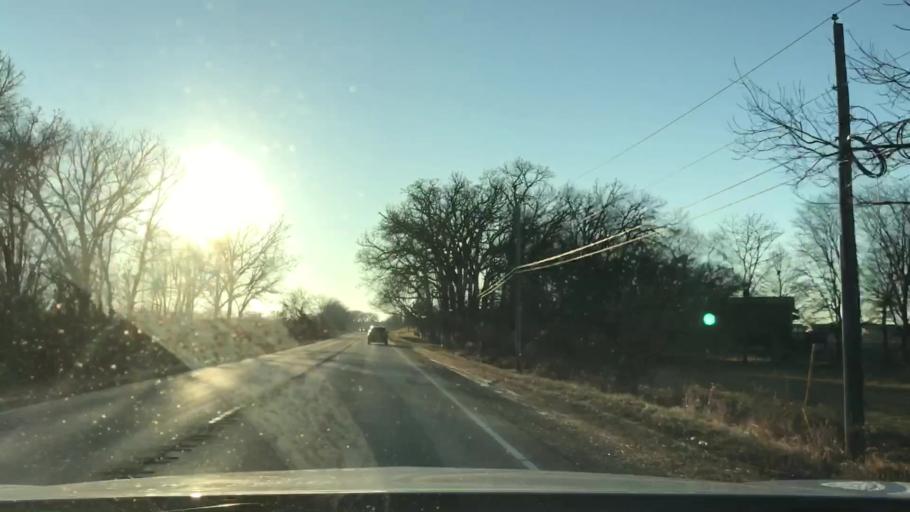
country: US
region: Illinois
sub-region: Kane County
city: Pingree Grove
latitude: 42.0928
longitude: -88.4173
